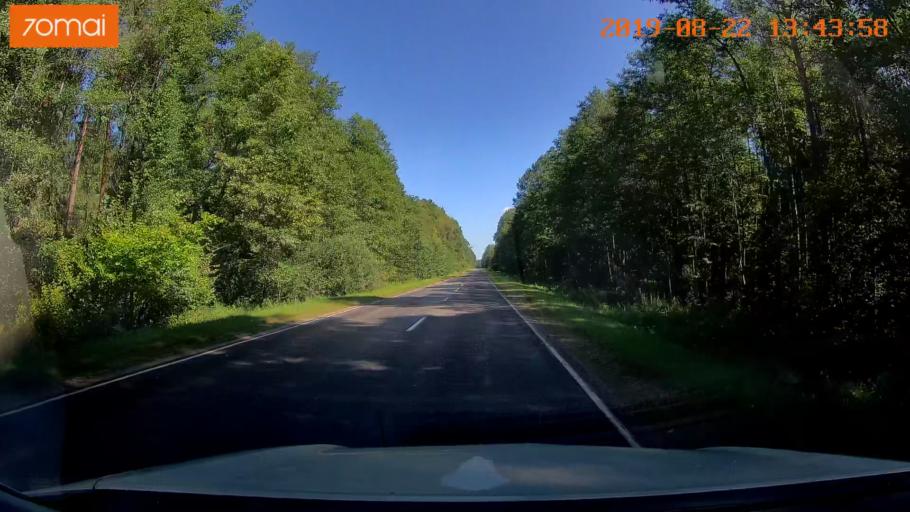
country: BY
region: Mogilev
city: Asipovichy
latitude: 53.2436
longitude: 28.4500
